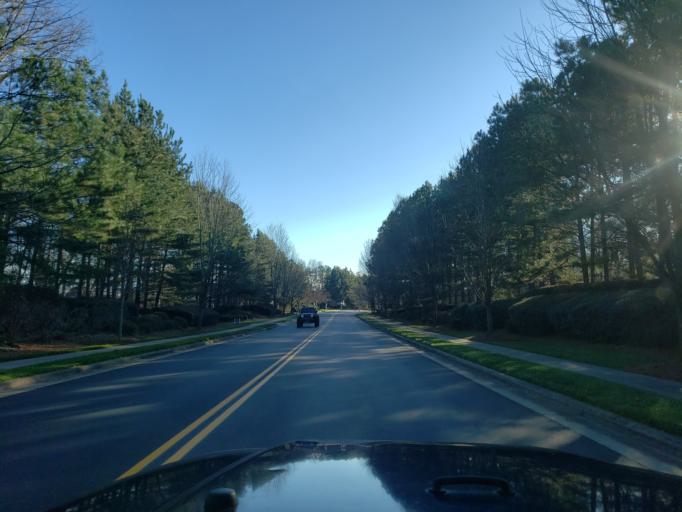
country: US
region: North Carolina
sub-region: Lincoln County
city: Westport
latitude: 35.5302
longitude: -80.9231
